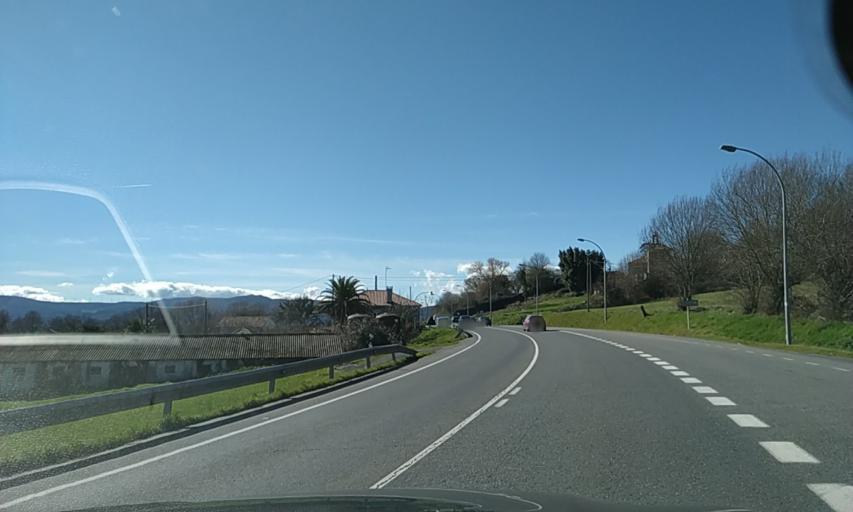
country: ES
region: Galicia
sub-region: Provincia de Pontevedra
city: Lalin
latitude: 42.6827
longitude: -8.1697
